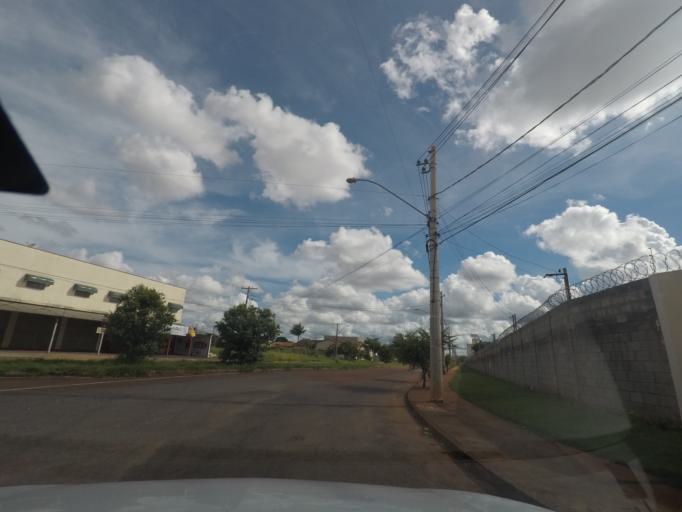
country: BR
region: Goias
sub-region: Goiania
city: Goiania
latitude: -16.7170
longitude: -49.3461
